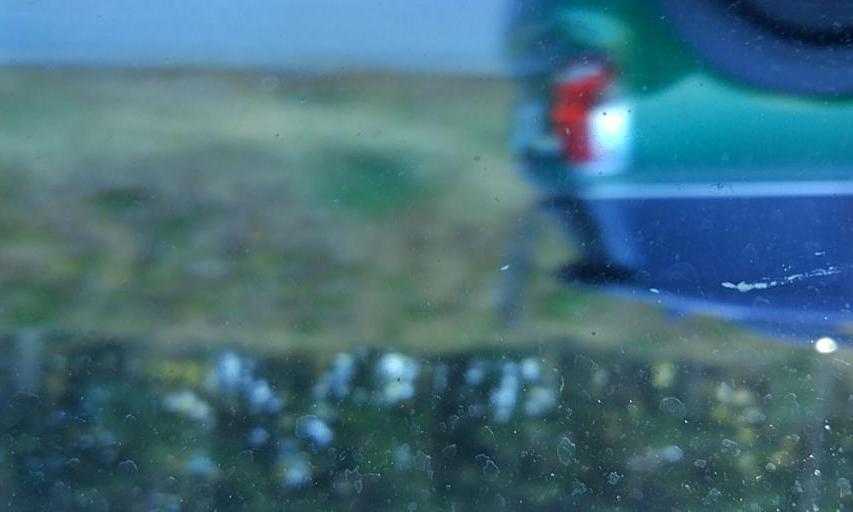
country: PT
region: Vila Real
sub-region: Sabrosa
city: Sabrosa
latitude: 41.3543
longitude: -7.5941
